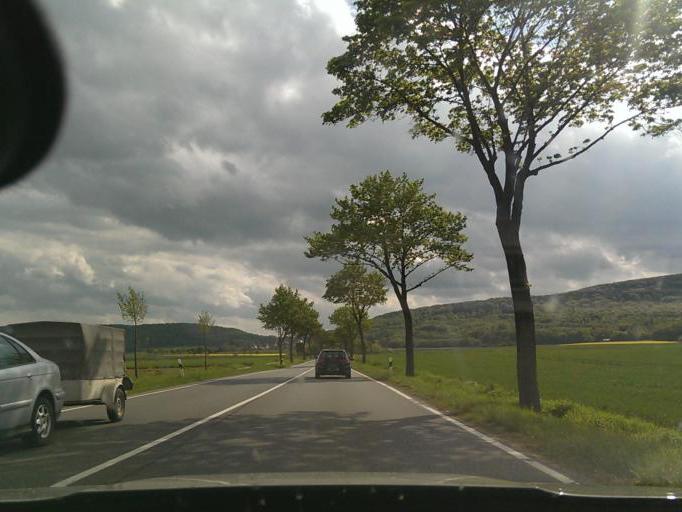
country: DE
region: Lower Saxony
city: Marienhagen
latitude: 52.0535
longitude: 9.6967
